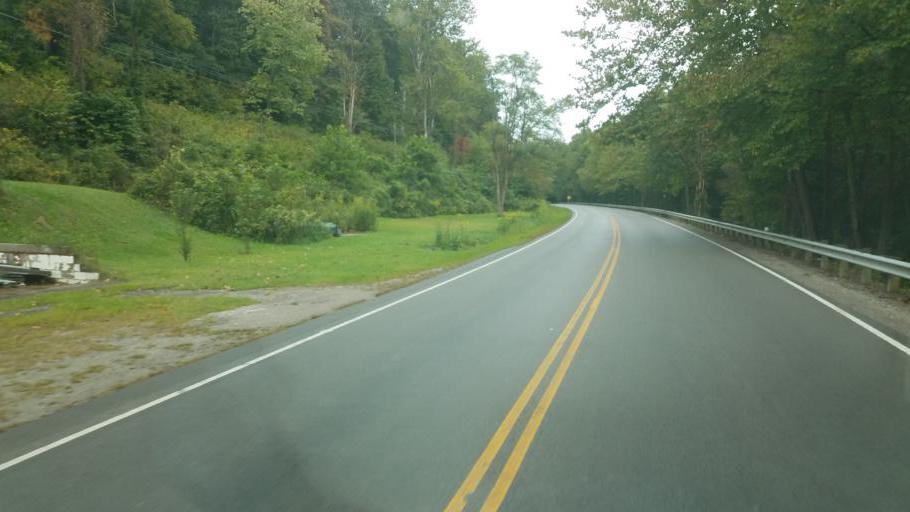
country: US
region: Ohio
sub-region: Scioto County
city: Sciotodale
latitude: 38.8047
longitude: -82.7645
